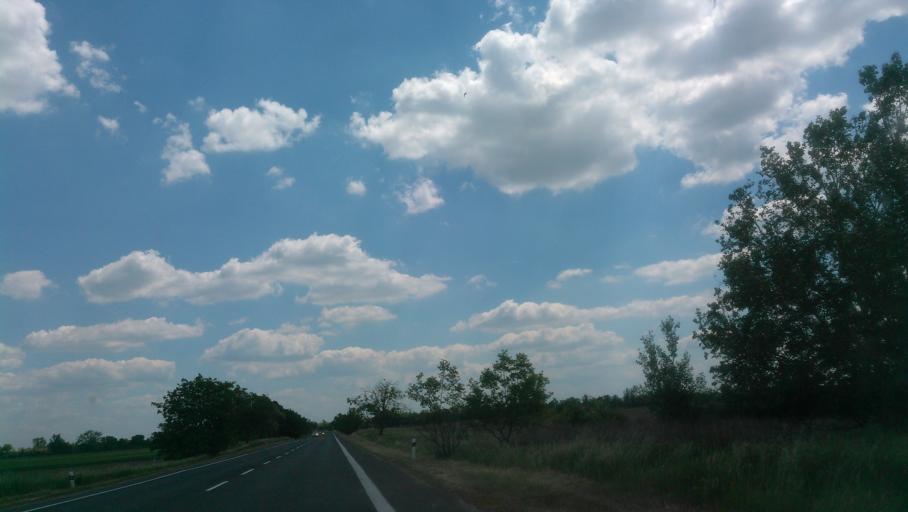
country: SK
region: Trnavsky
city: Samorin
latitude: 48.0505
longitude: 17.2907
